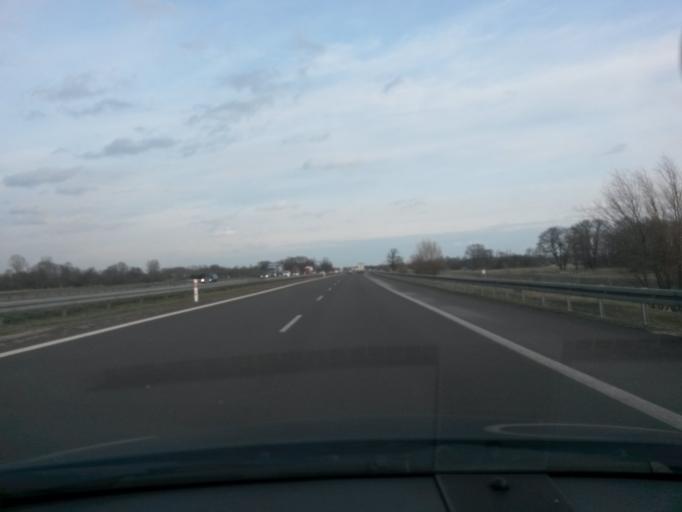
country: PL
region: Greater Poland Voivodeship
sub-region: Powiat turecki
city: Brudzew
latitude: 52.1276
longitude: 18.6676
